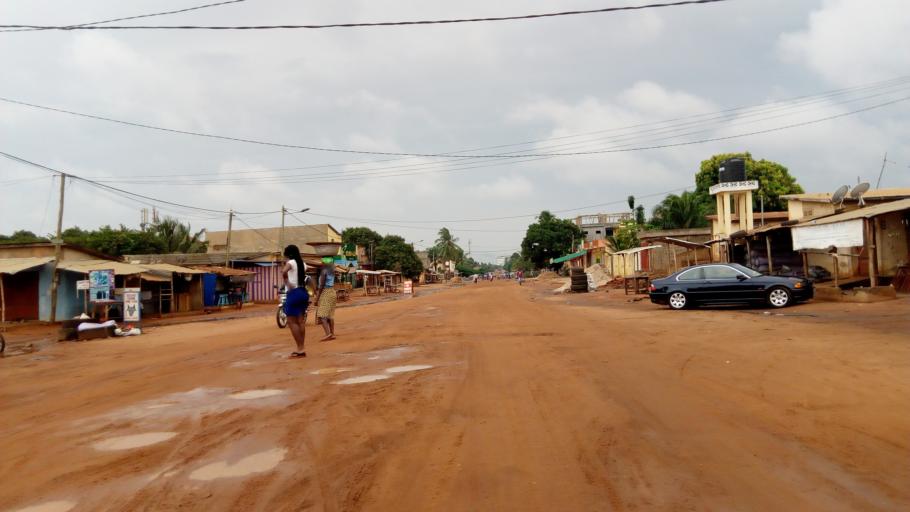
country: TG
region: Maritime
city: Lome
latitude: 6.2314
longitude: 1.1803
